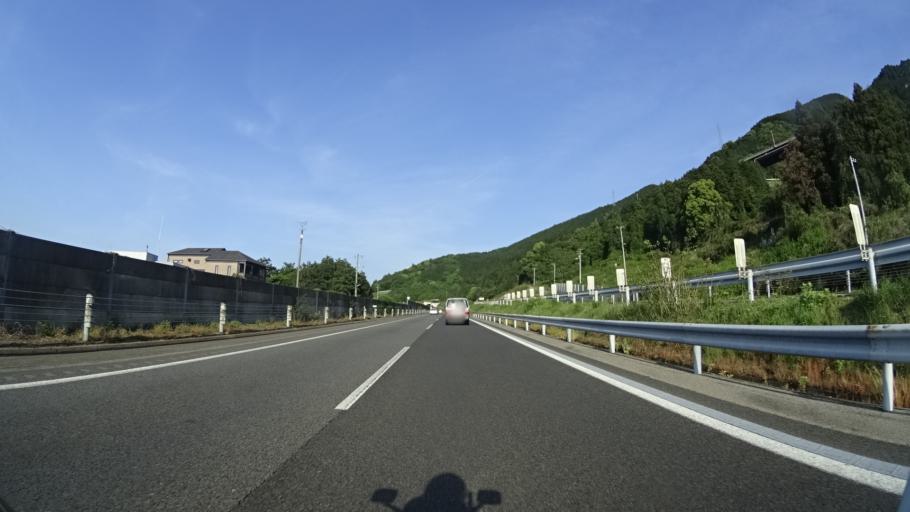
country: JP
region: Ehime
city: Kawanoecho
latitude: 33.9645
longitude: 133.5322
